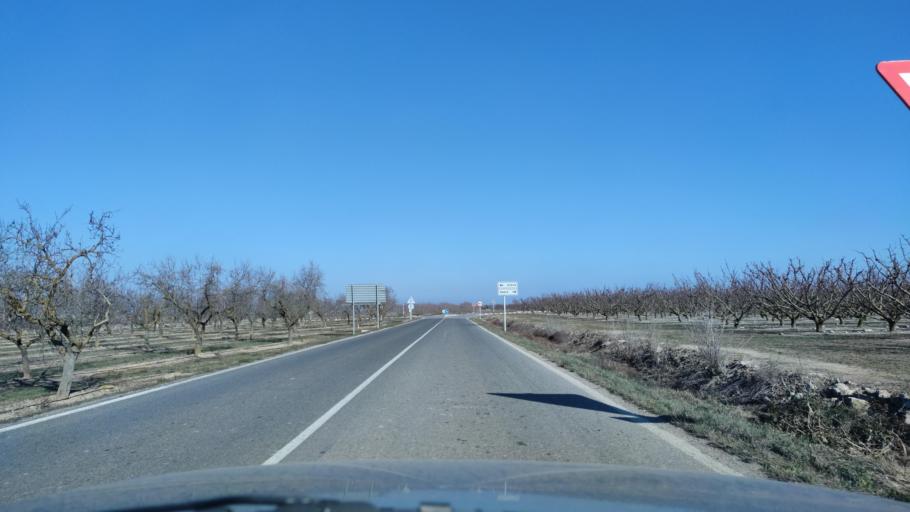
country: ES
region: Catalonia
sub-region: Provincia de Lleida
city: Maials
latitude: 41.3663
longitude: 0.4953
